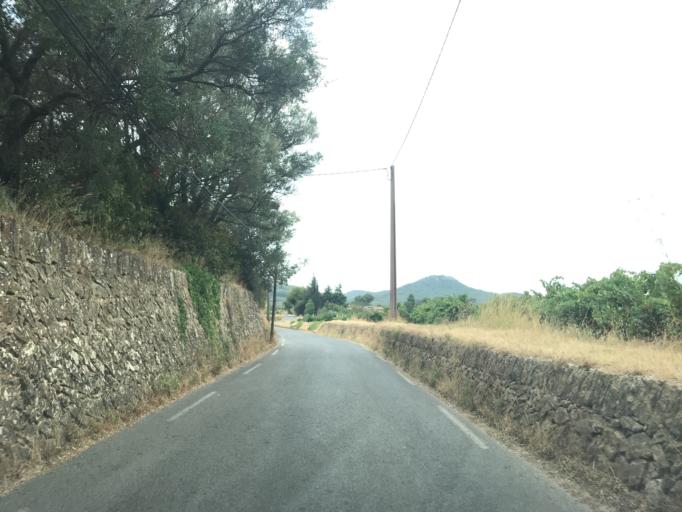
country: FR
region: Provence-Alpes-Cote d'Azur
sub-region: Departement du Var
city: Saint-Cyr-sur-Mer
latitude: 43.1809
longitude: 5.7332
